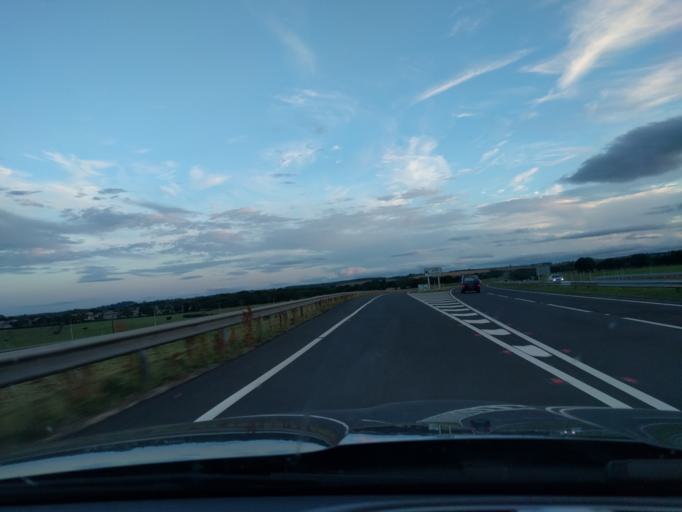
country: GB
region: England
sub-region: Northumberland
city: Morpeth
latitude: 55.1798
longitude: -1.7161
